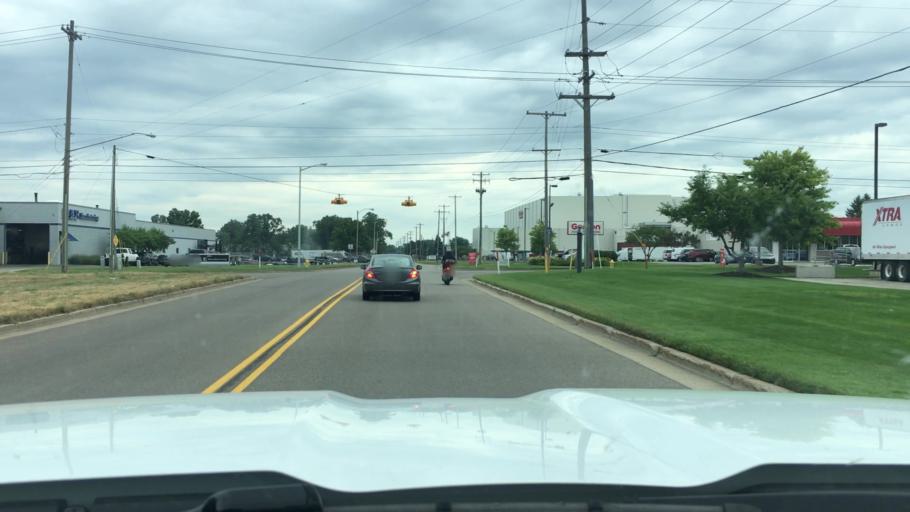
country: US
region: Michigan
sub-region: Kent County
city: Kentwood
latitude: 42.8728
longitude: -85.6777
